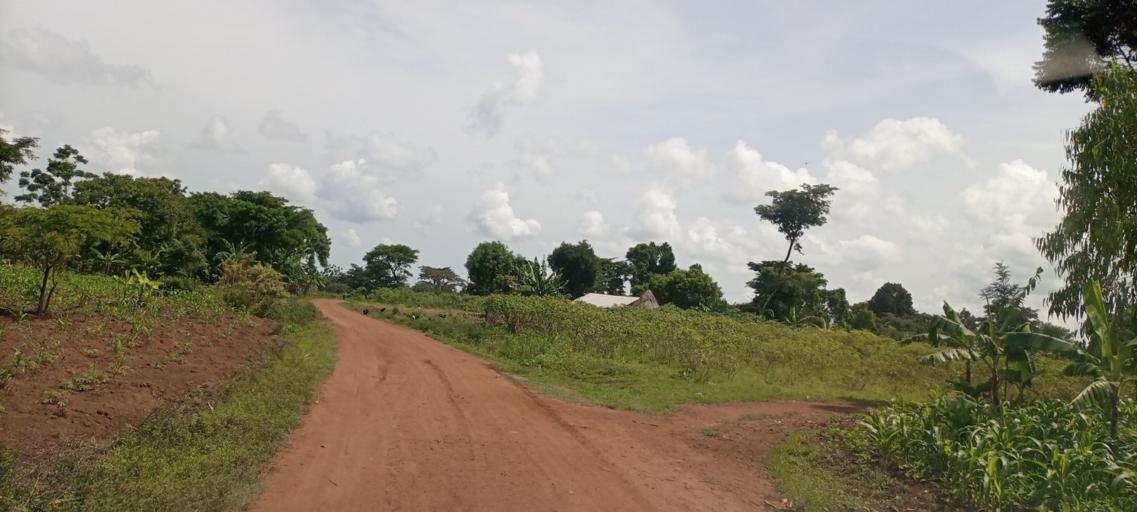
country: UG
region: Eastern Region
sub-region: Budaka District
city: Budaka
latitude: 1.1763
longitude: 33.9234
